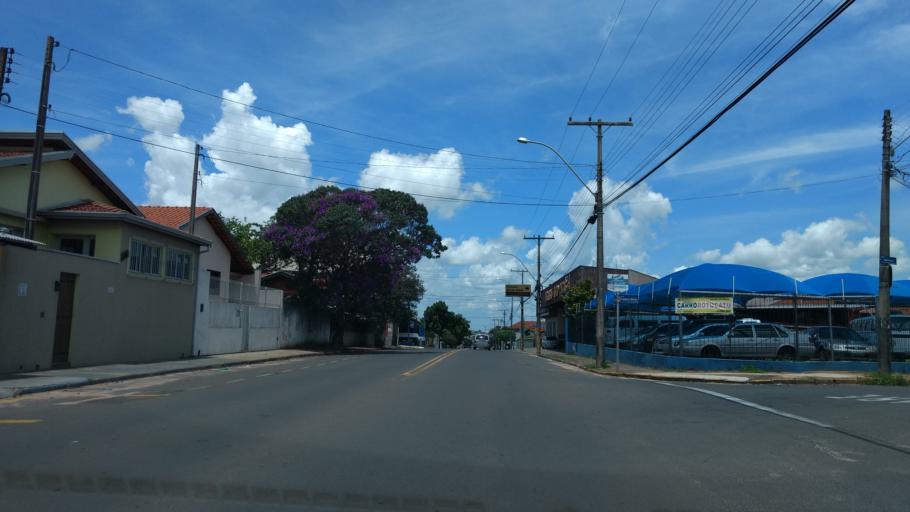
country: BR
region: Sao Paulo
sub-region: Botucatu
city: Botucatu
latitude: -22.8697
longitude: -48.4579
